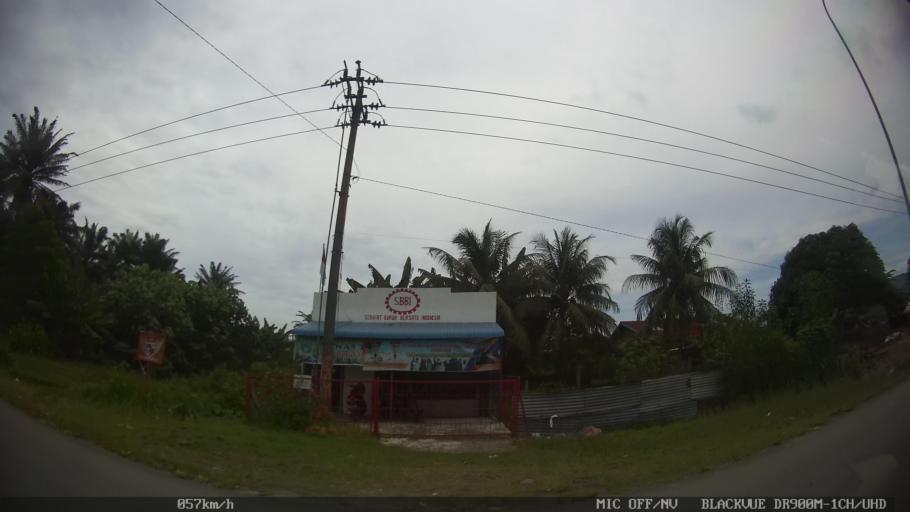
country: ID
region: North Sumatra
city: Sunggal
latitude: 3.6181
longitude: 98.5760
